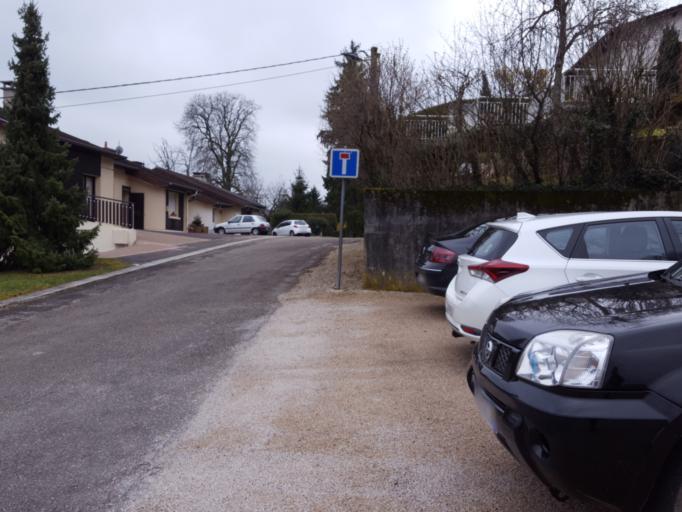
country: FR
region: Franche-Comte
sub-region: Departement du Jura
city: Lons-le-Saunier
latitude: 46.6656
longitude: 5.5401
